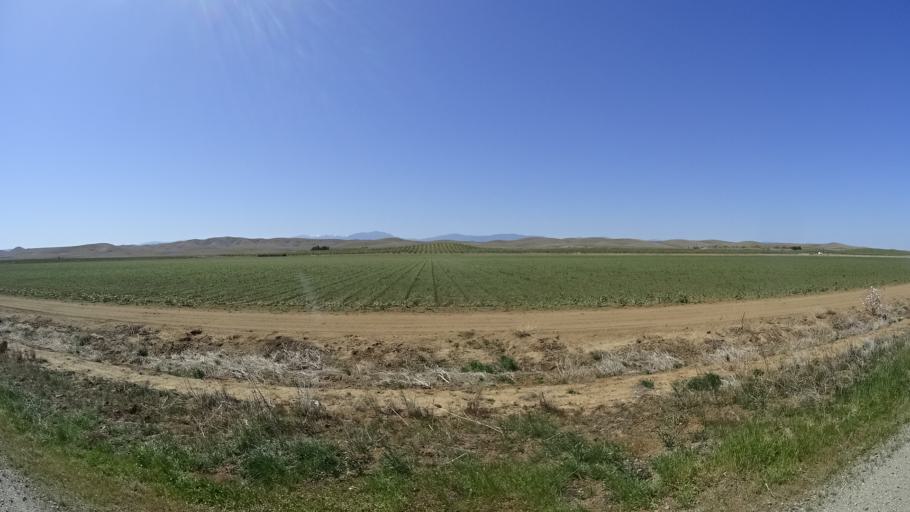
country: US
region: California
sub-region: Glenn County
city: Willows
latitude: 39.4751
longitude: -122.2866
